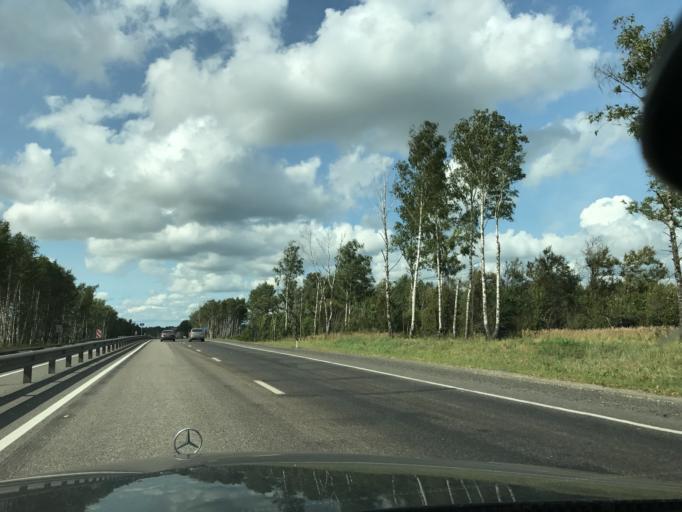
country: RU
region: Vladimir
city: Novovyazniki
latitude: 56.1960
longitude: 42.3718
